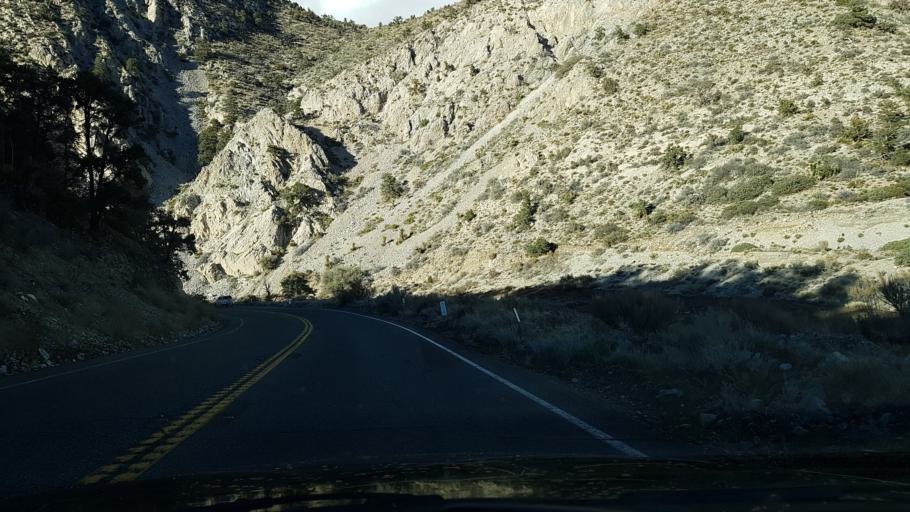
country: US
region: California
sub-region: San Bernardino County
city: Big Bear City
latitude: 34.3365
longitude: -116.8343
